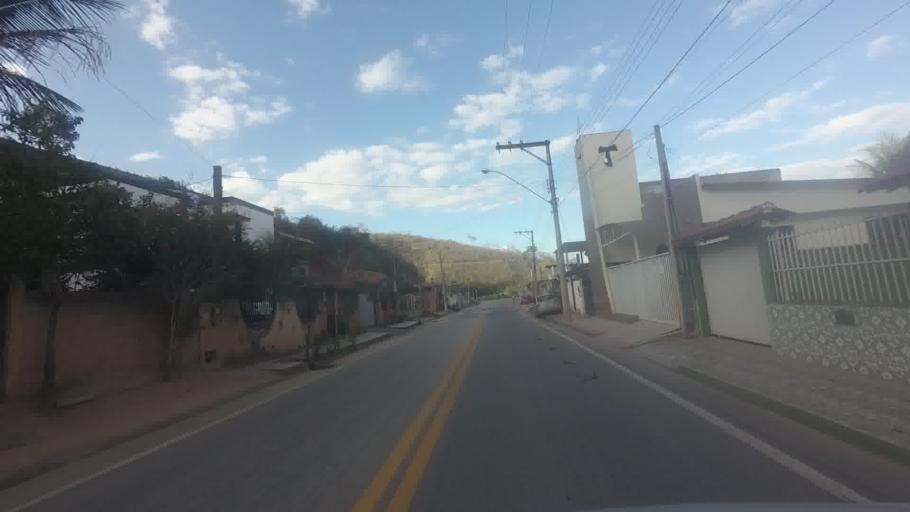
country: BR
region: Espirito Santo
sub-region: Mimoso Do Sul
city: Mimoso do Sul
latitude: -20.9416
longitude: -41.3321
